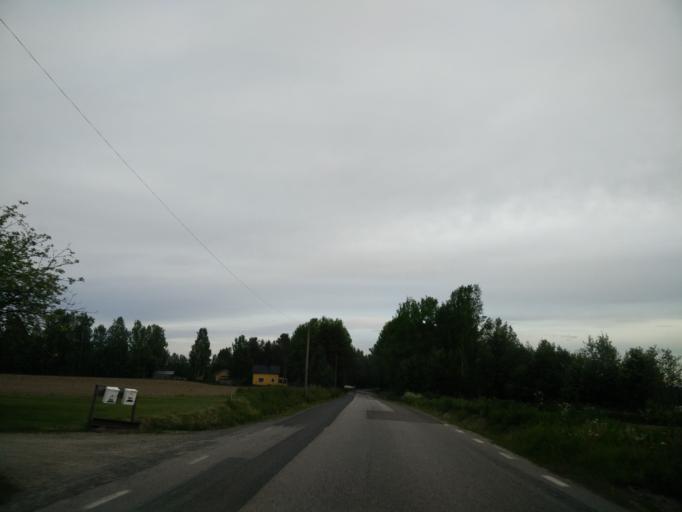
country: SE
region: Vaesternorrland
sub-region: Kramfors Kommun
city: Kramfors
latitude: 63.0341
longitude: 17.7897
